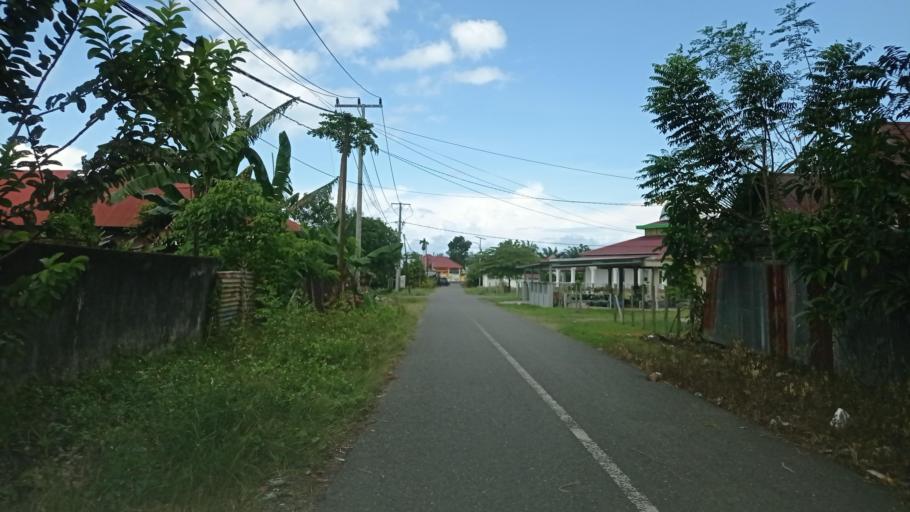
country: ID
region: Jambi
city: Sungai Penuh
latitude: -2.5596
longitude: 101.1050
